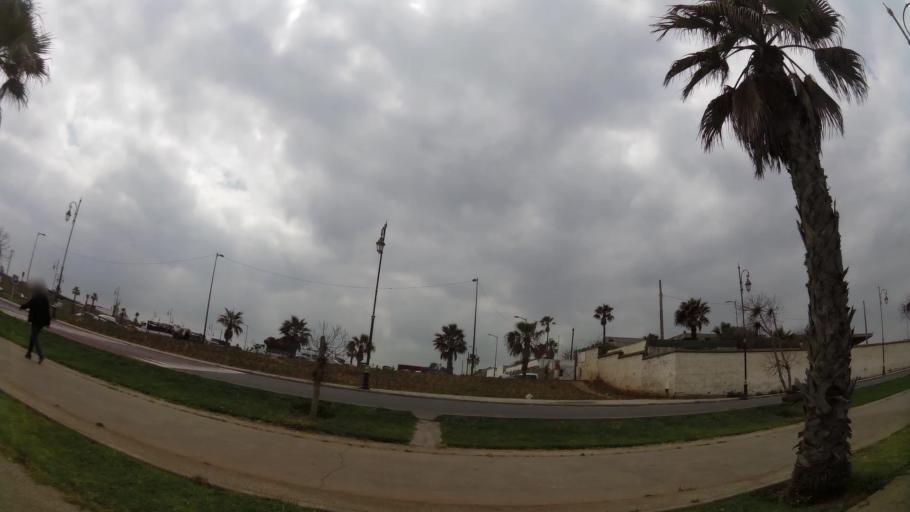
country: MA
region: Rabat-Sale-Zemmour-Zaer
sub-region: Rabat
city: Rabat
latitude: 34.0077
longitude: -6.8675
